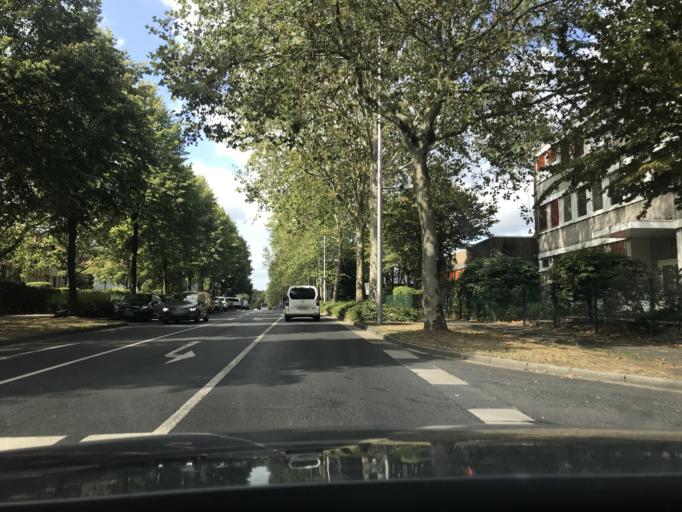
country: DE
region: North Rhine-Westphalia
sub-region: Regierungsbezirk Dusseldorf
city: Erkrath
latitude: 51.2154
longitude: 6.9481
